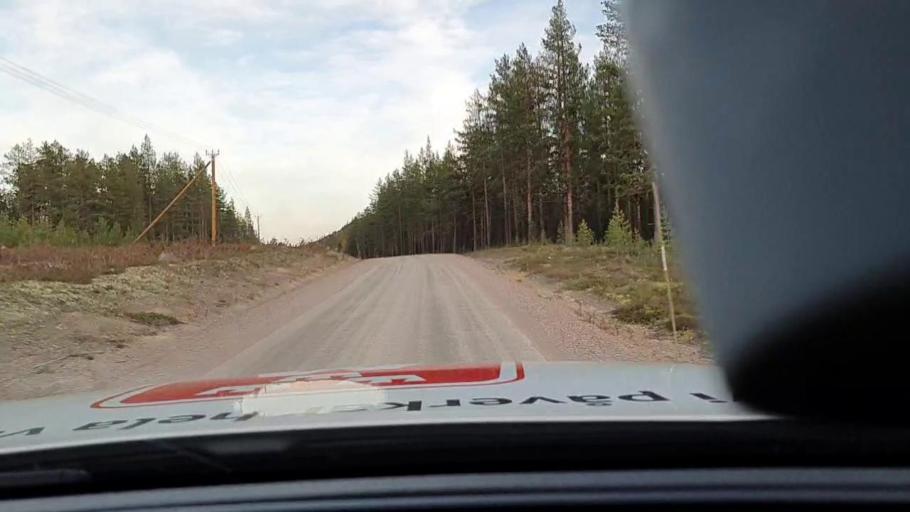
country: SE
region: Norrbotten
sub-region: Overkalix Kommun
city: OEverkalix
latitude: 66.3282
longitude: 22.5935
